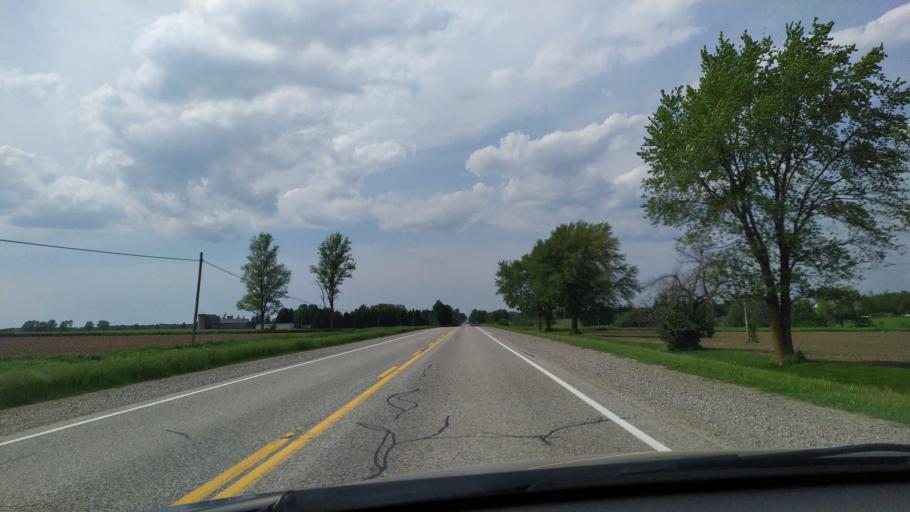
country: CA
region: Ontario
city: Dorchester
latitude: 43.1272
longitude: -81.0241
